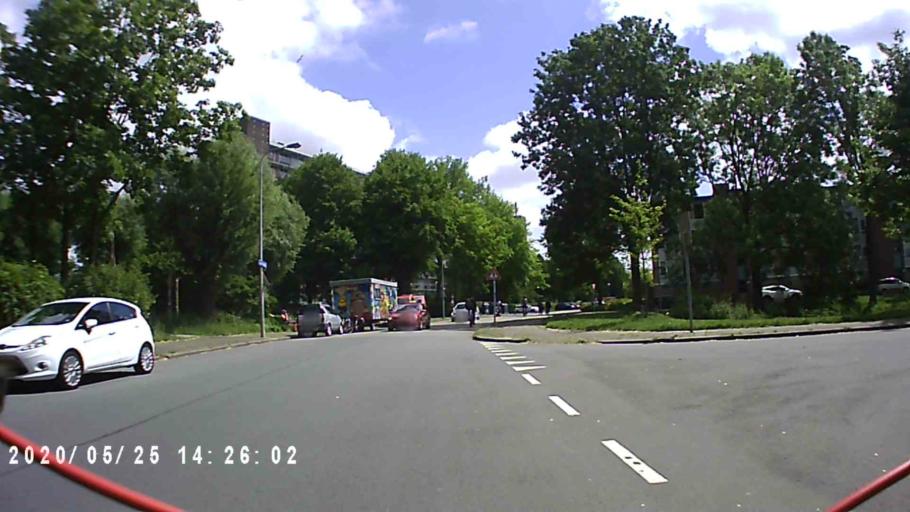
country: NL
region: Groningen
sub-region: Gemeente Groningen
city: Groningen
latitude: 53.2296
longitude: 6.5301
